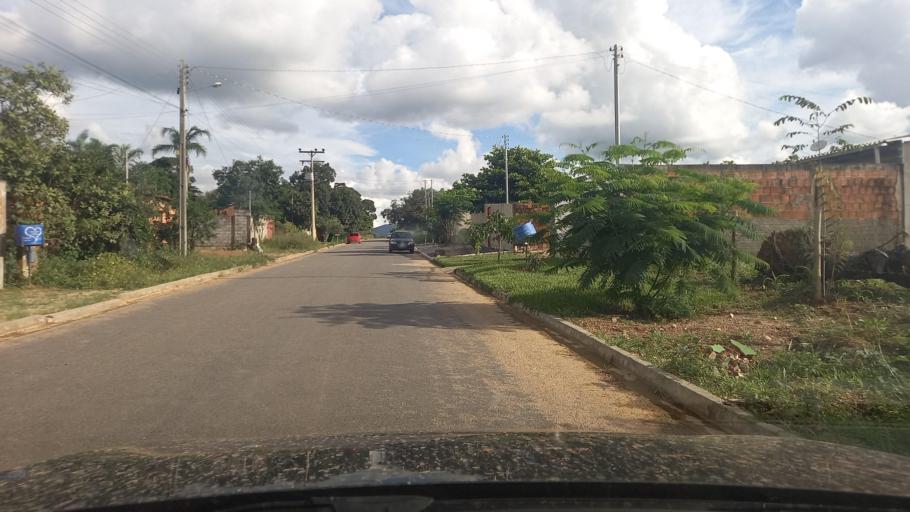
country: BR
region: Goias
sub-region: Cavalcante
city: Cavalcante
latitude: -13.7970
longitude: -47.4467
